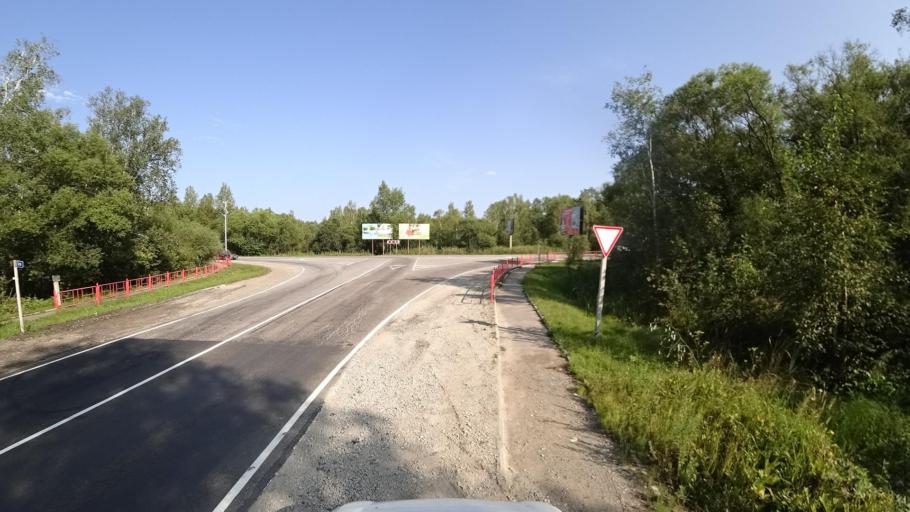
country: RU
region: Khabarovsk Krai
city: Khor
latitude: 47.9748
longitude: 135.0821
